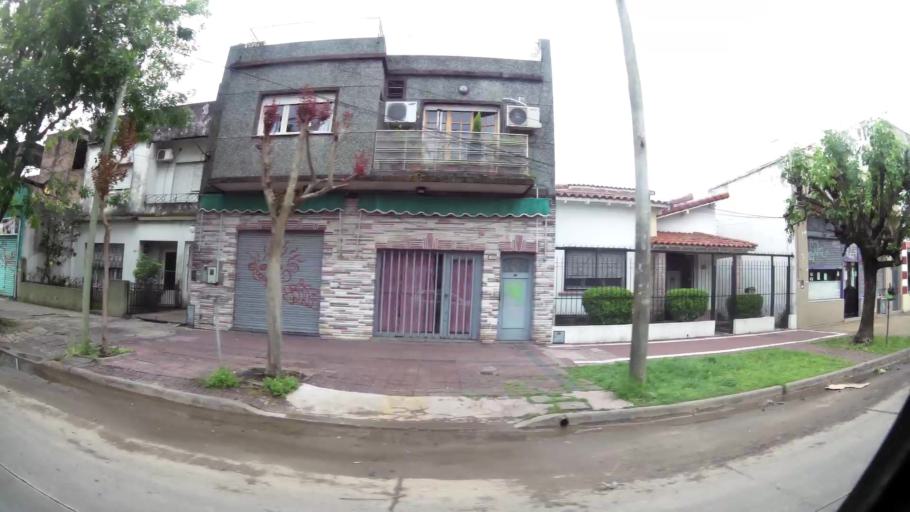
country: AR
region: Buenos Aires
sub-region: Partido de Lanus
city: Lanus
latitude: -34.7155
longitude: -58.3748
